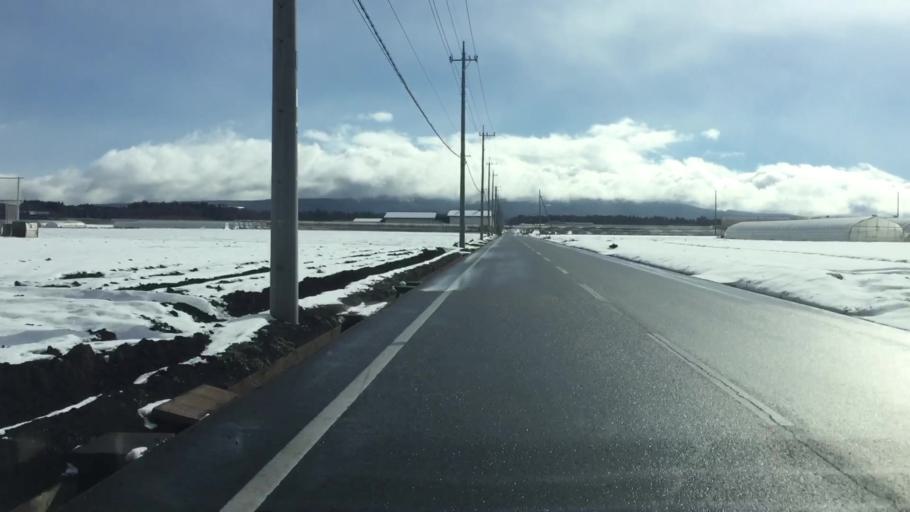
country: JP
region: Gunma
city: Numata
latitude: 36.6343
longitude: 139.0853
